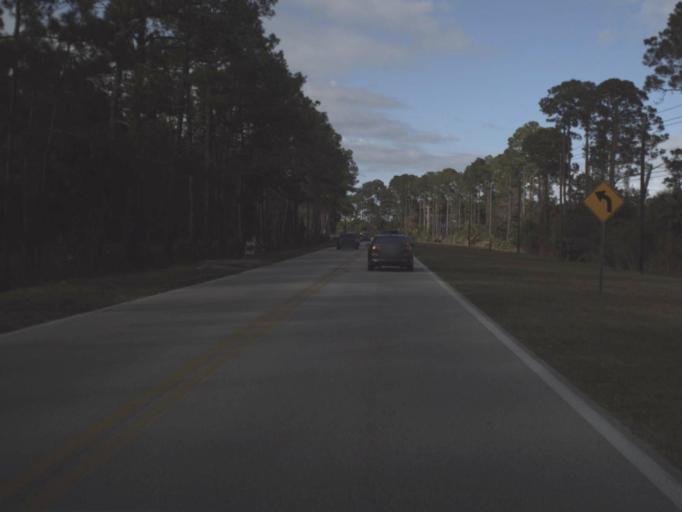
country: US
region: Florida
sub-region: Volusia County
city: Holly Hill
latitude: 29.2380
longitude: -81.0985
